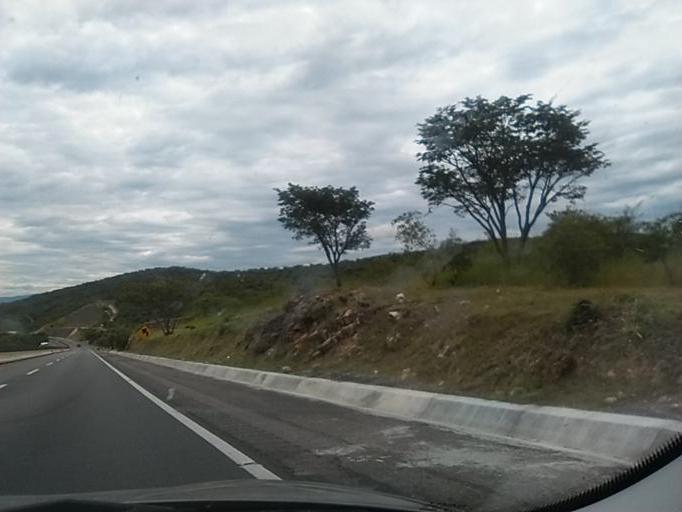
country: MX
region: Guerrero
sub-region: Huitzuco de los Figueroa
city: Ciudad de Huitzuco
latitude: 18.1518
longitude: -99.2127
